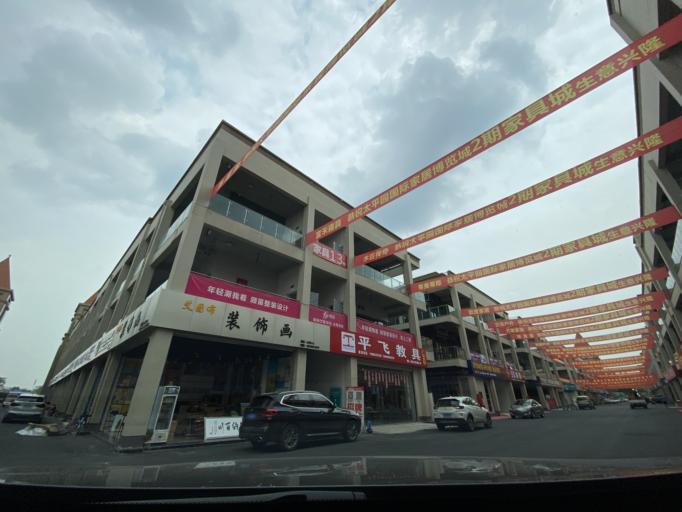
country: CN
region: Sichuan
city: Dongsheng
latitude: 30.6102
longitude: 103.9407
